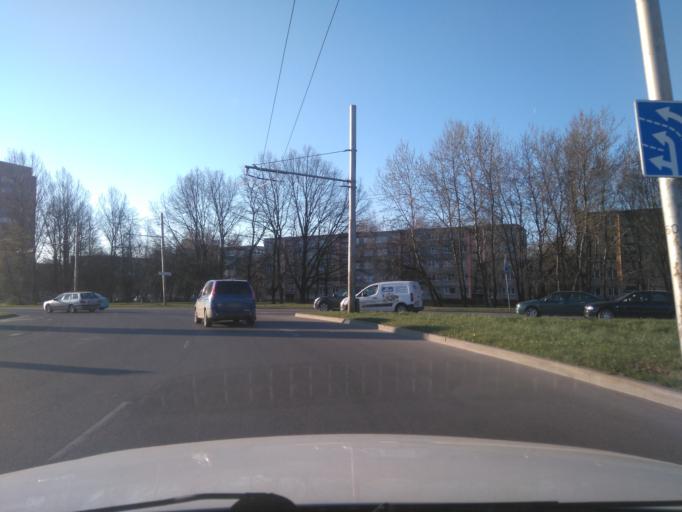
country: LT
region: Kauno apskritis
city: Dainava (Kaunas)
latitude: 54.9121
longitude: 23.9718
